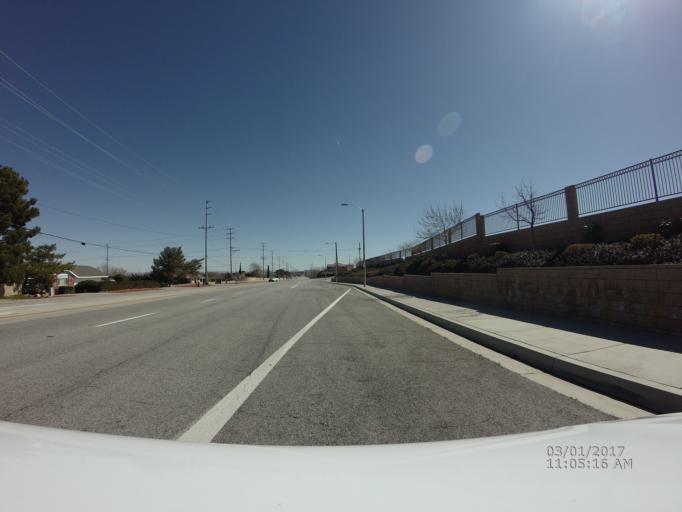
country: US
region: California
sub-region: Los Angeles County
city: Quartz Hill
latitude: 34.6454
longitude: -118.2550
